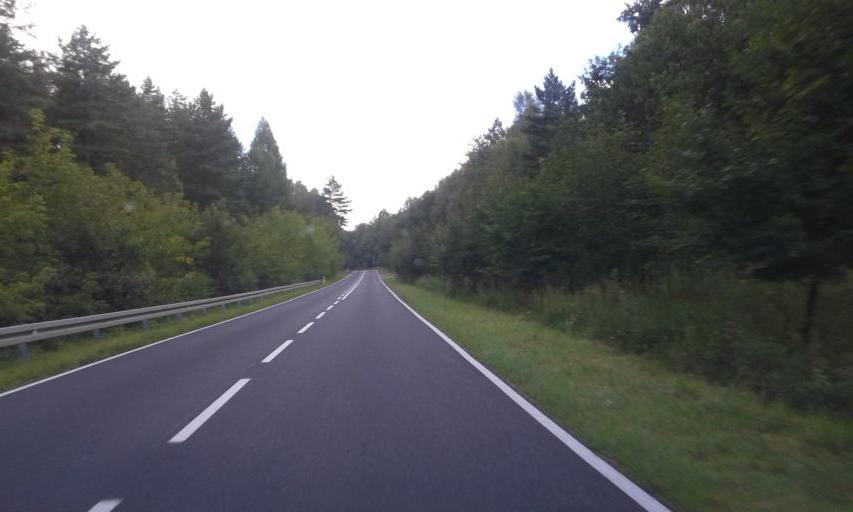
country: PL
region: West Pomeranian Voivodeship
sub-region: Powiat koszalinski
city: Polanow
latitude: 54.0210
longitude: 16.7238
